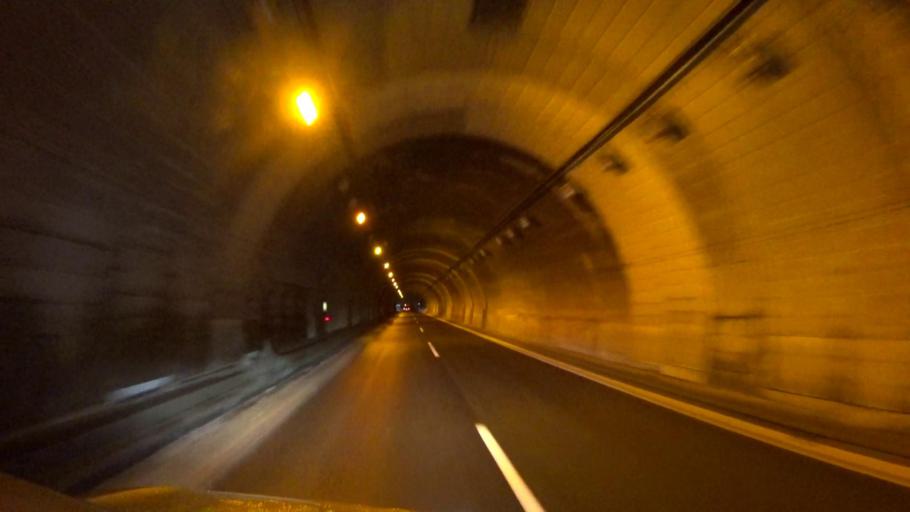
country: JP
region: Hokkaido
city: Otaru
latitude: 43.1749
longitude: 141.0288
